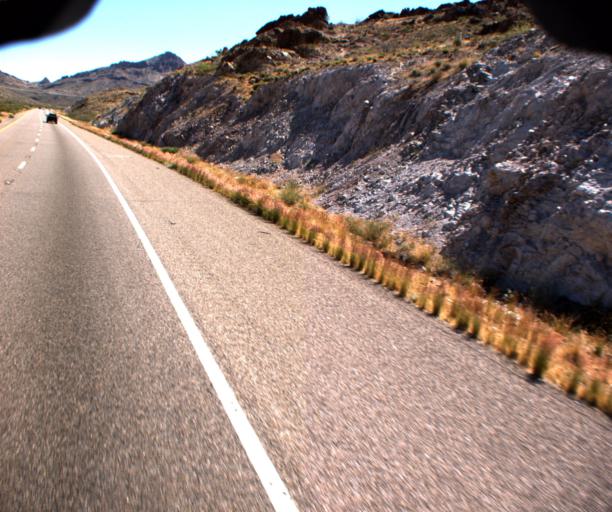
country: US
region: Nevada
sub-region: Clark County
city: Laughlin
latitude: 35.1965
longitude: -114.4305
